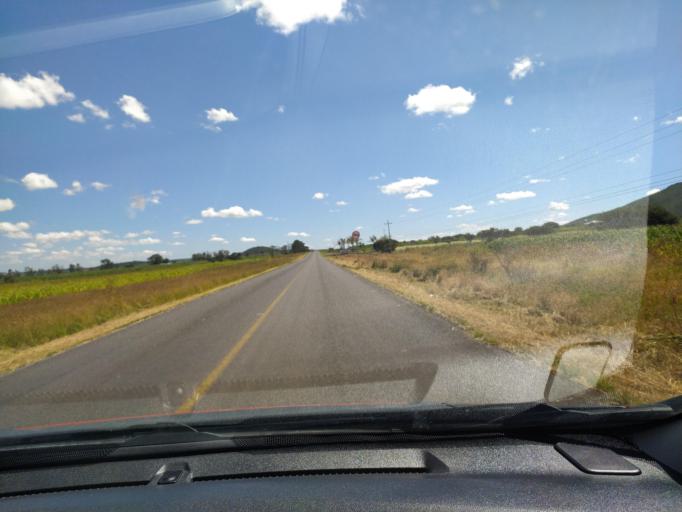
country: MX
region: Jalisco
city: San Miguel el Alto
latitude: 21.0165
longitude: -102.4719
